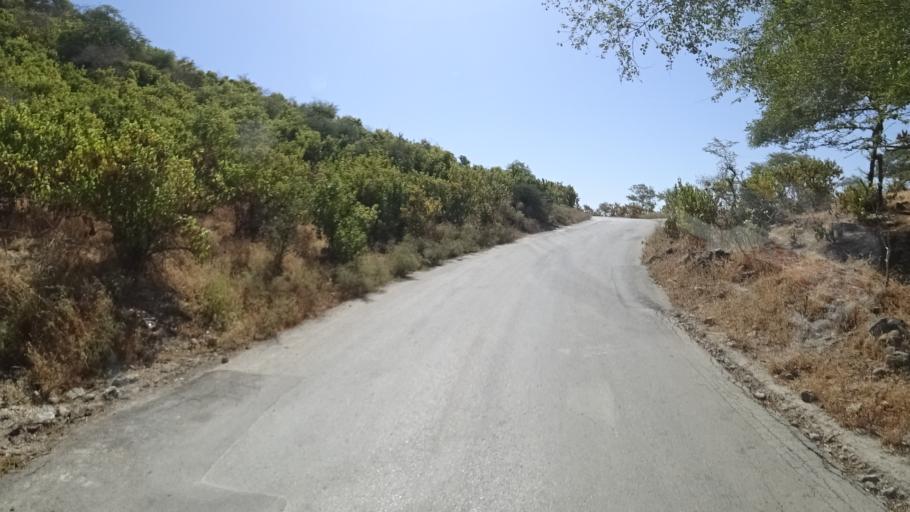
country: OM
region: Zufar
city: Salalah
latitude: 17.0741
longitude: 54.4404
